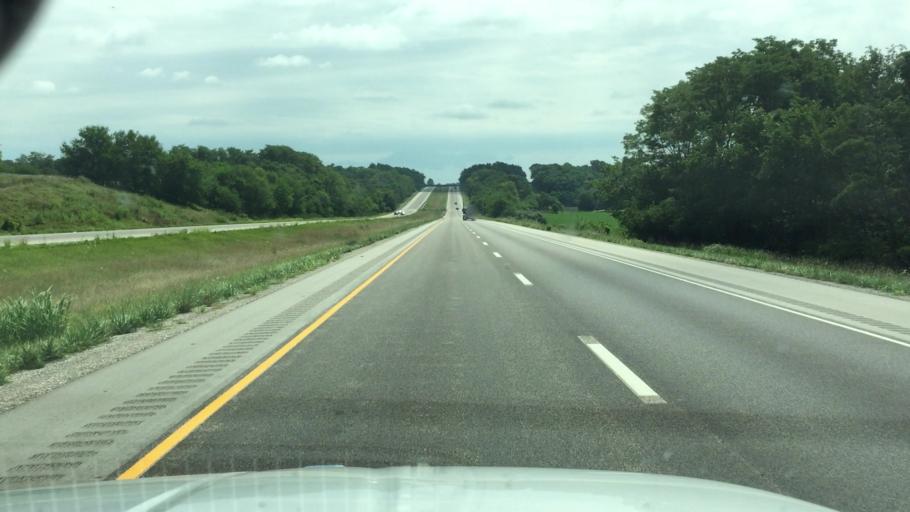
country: US
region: Illinois
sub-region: Peoria County
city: Elmwood
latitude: 40.8618
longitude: -90.0146
